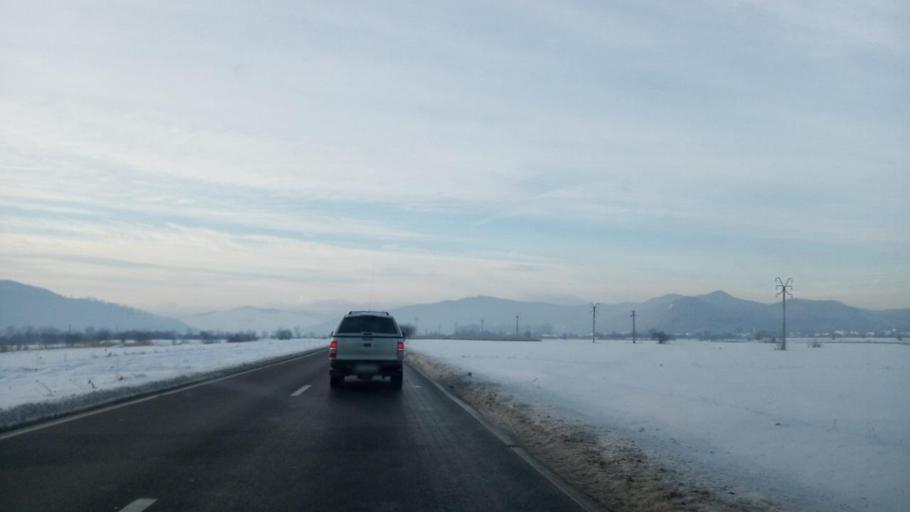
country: RO
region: Suceava
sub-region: Comuna Paltinoasa
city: Paltinoasa
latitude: 47.5381
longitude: 25.9631
